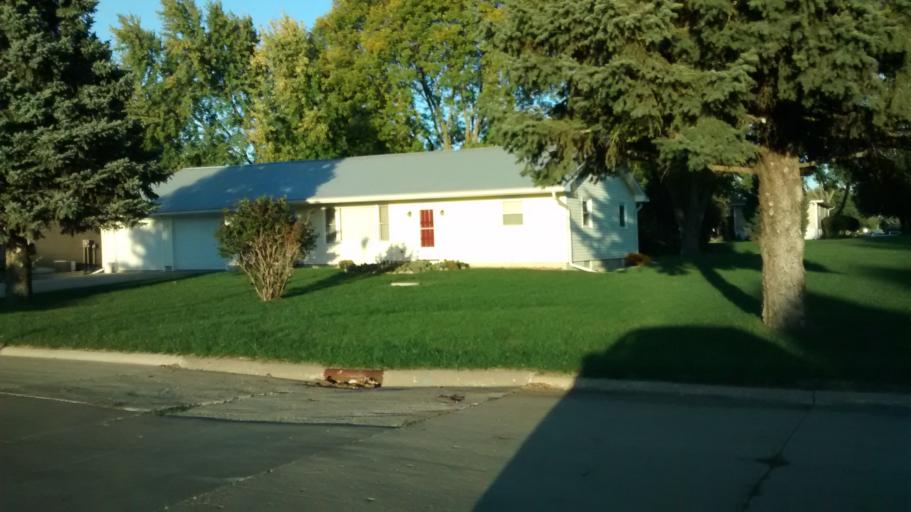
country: US
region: Iowa
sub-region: Woodbury County
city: Moville
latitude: 42.4903
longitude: -96.0667
